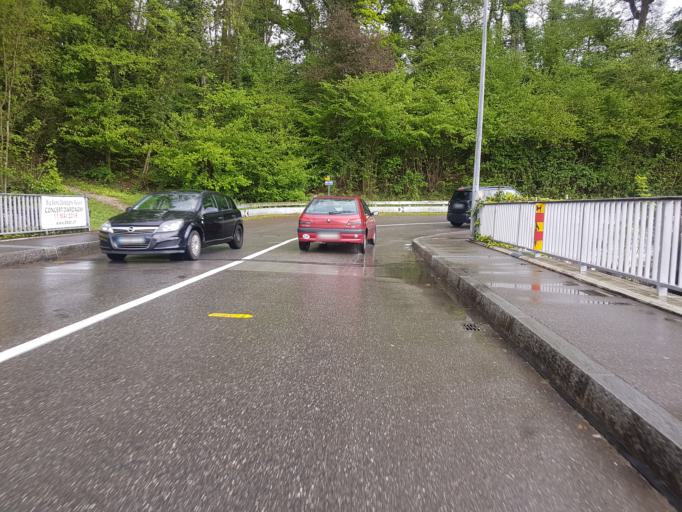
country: CH
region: Geneva
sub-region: Geneva
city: Dardagny
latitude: 46.1755
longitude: 6.0005
